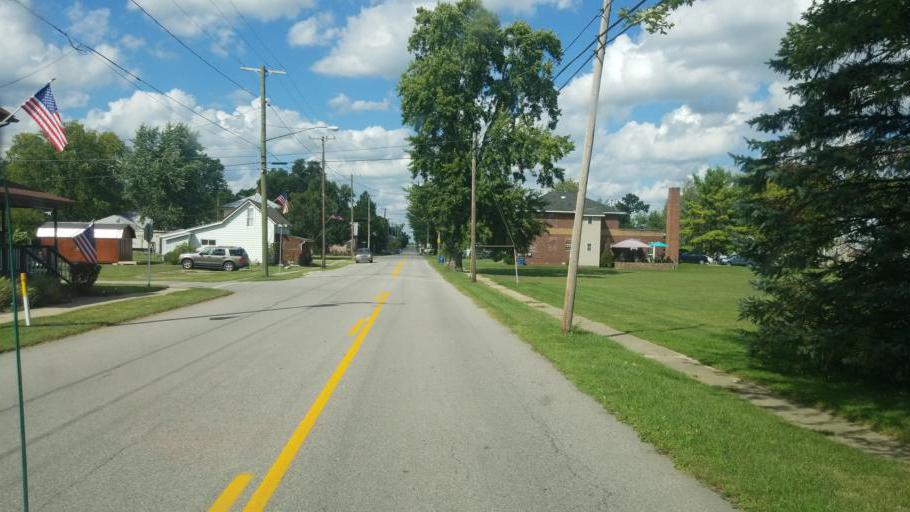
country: US
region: Ohio
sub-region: Union County
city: Richwood
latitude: 40.3514
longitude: -83.2630
